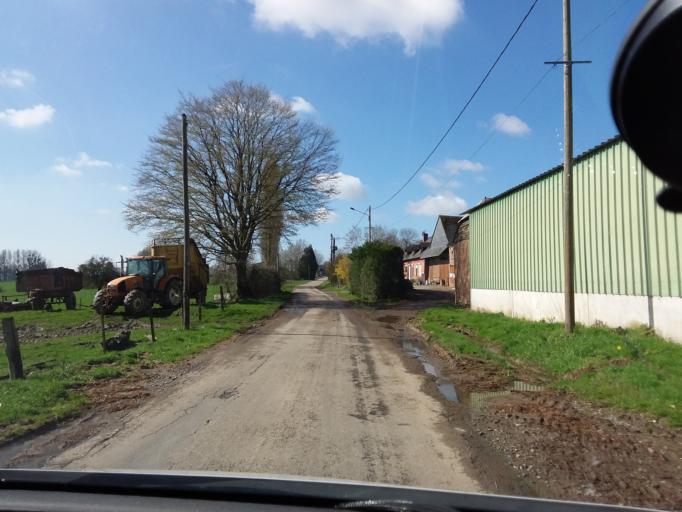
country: FR
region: Picardie
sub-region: Departement de l'Aisne
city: Origny-en-Thierache
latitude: 49.8293
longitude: 4.0496
